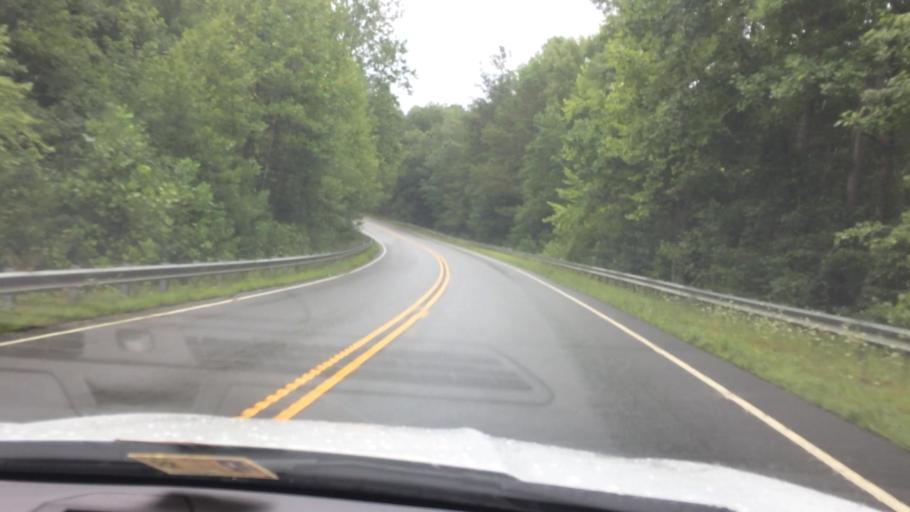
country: US
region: Virginia
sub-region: King William County
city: West Point
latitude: 37.5582
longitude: -76.7445
